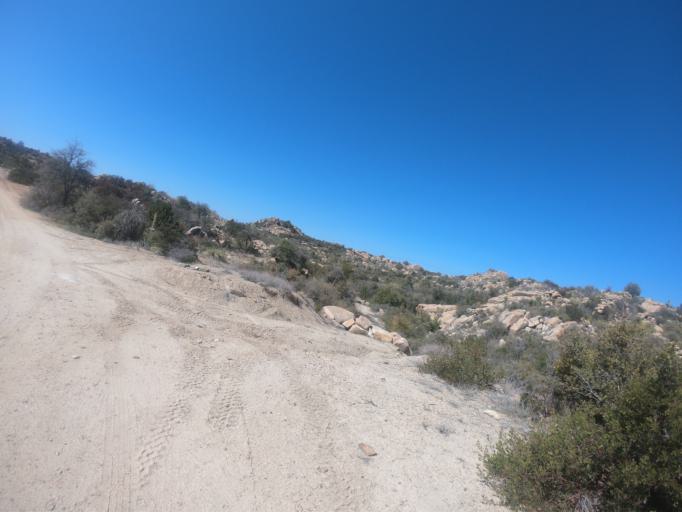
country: US
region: Arizona
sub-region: Gila County
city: Miami
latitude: 33.3550
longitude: -110.9666
